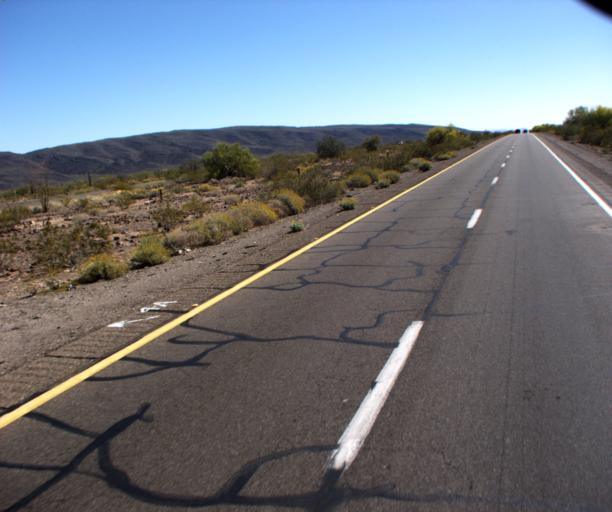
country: US
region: Arizona
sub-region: La Paz County
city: Quartzsite
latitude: 33.6540
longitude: -113.9486
